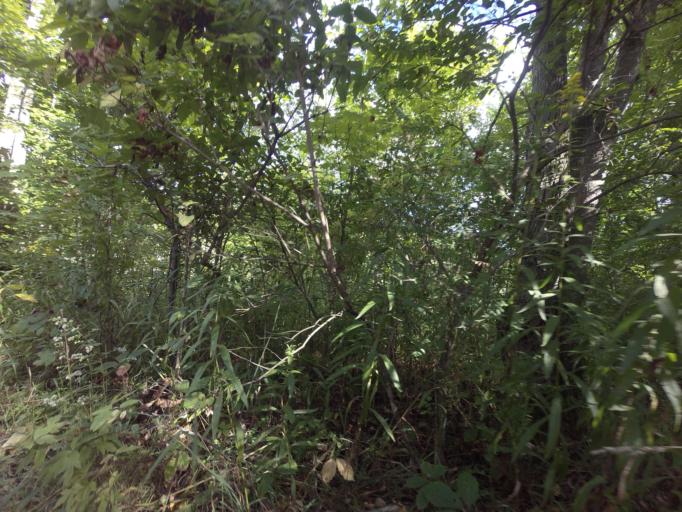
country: CA
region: Ontario
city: Orangeville
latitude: 43.8233
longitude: -80.0076
